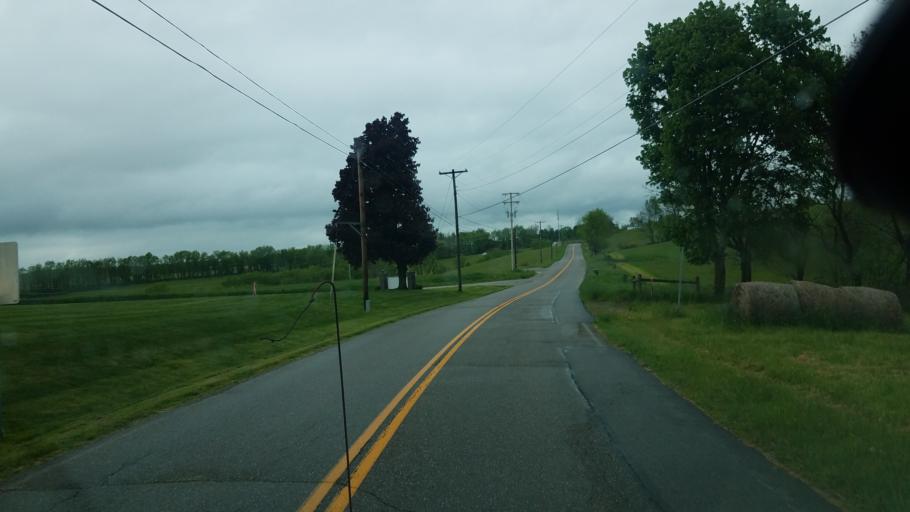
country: US
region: Ohio
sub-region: Jefferson County
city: Tiltonsville
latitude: 40.2499
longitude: -80.7507
